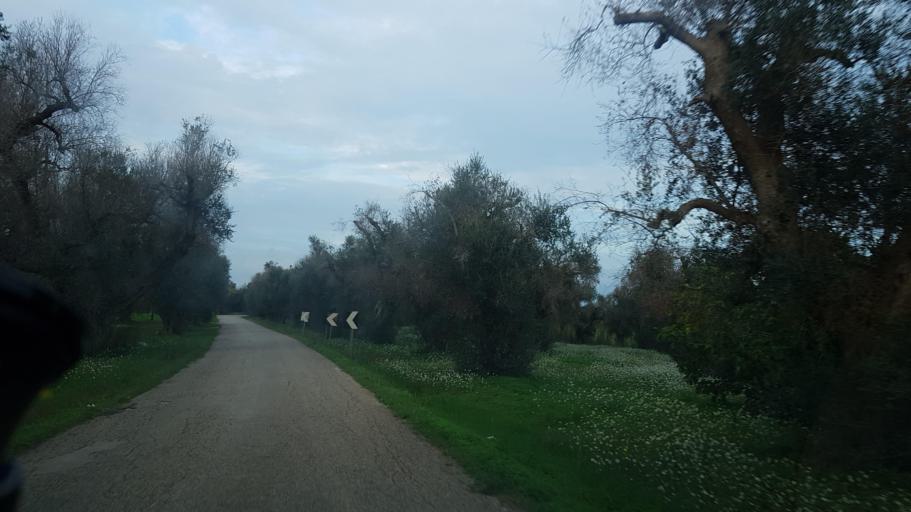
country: IT
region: Apulia
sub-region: Provincia di Brindisi
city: Mesagne
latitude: 40.5404
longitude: 17.7809
